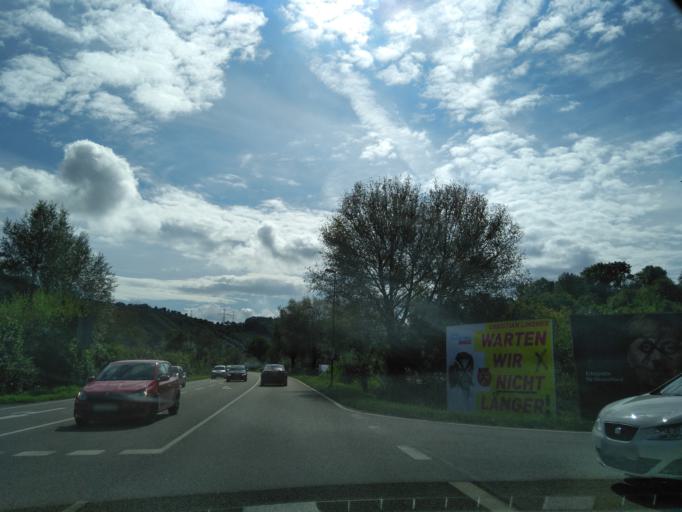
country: DE
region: Baden-Wuerttemberg
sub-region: Regierungsbezirk Stuttgart
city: Besigheim
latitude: 48.9930
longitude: 9.1452
